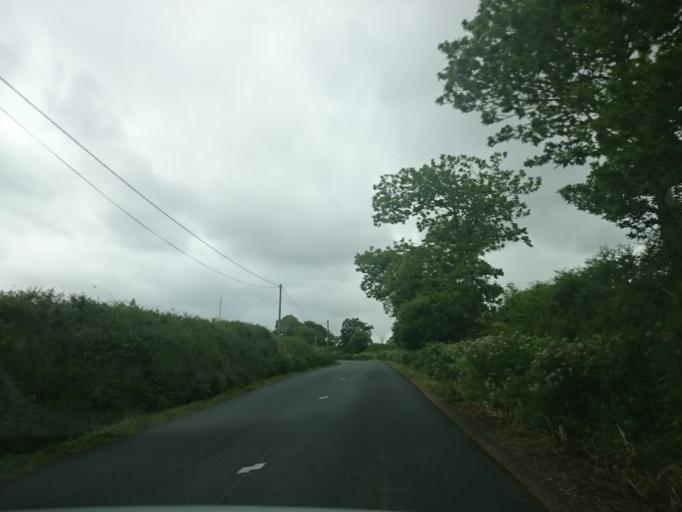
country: FR
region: Brittany
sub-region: Departement des Cotes-d'Armor
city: Rospez
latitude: 48.7618
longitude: -3.3933
